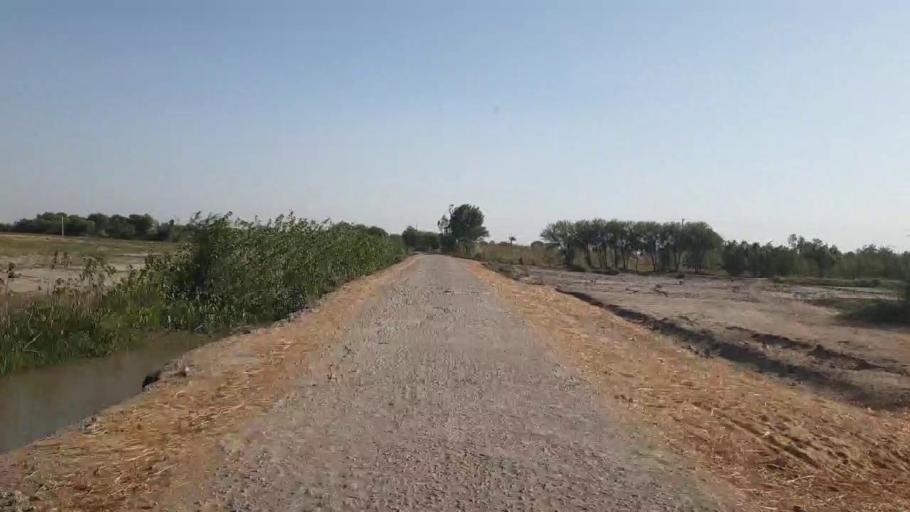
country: PK
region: Sindh
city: Matli
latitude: 25.0369
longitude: 68.7288
